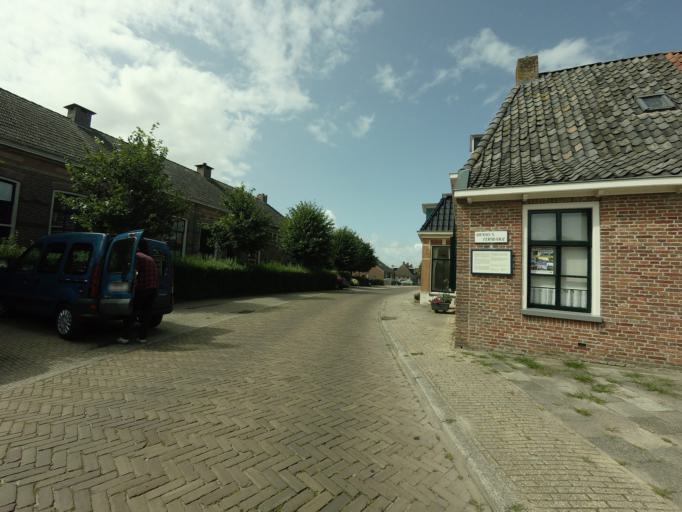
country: NL
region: Friesland
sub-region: Gemeente Harlingen
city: Harlingen
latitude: 53.1157
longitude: 5.4389
